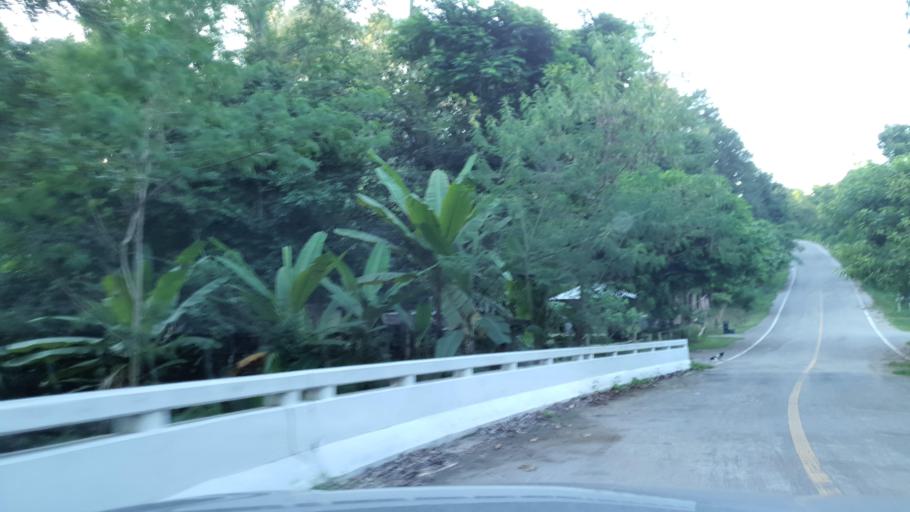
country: TH
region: Chiang Mai
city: Mae On
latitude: 18.8189
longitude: 99.3022
